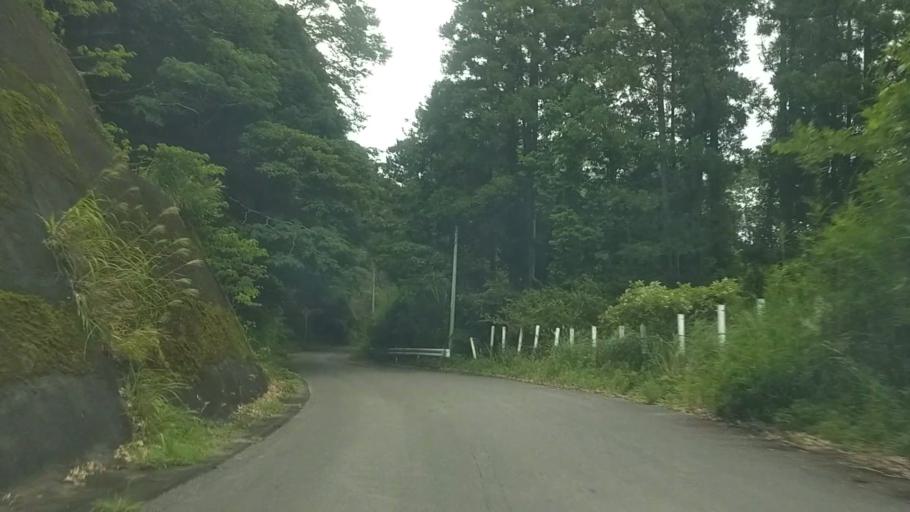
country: JP
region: Chiba
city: Kawaguchi
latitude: 35.2521
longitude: 140.0720
